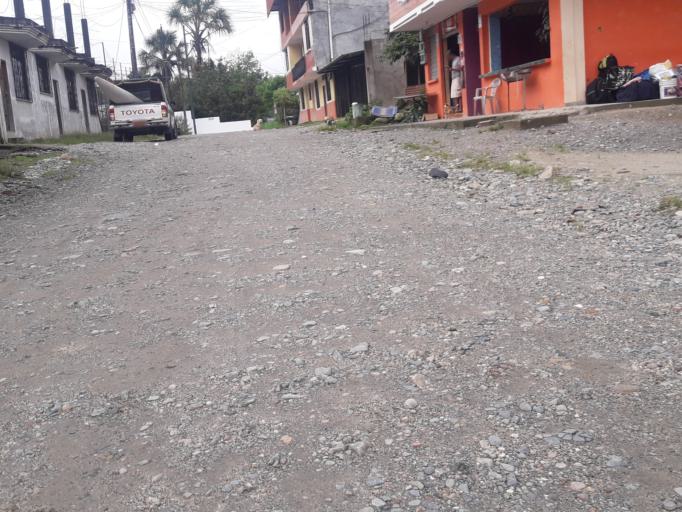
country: EC
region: Napo
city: Tena
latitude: -1.0002
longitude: -77.8083
